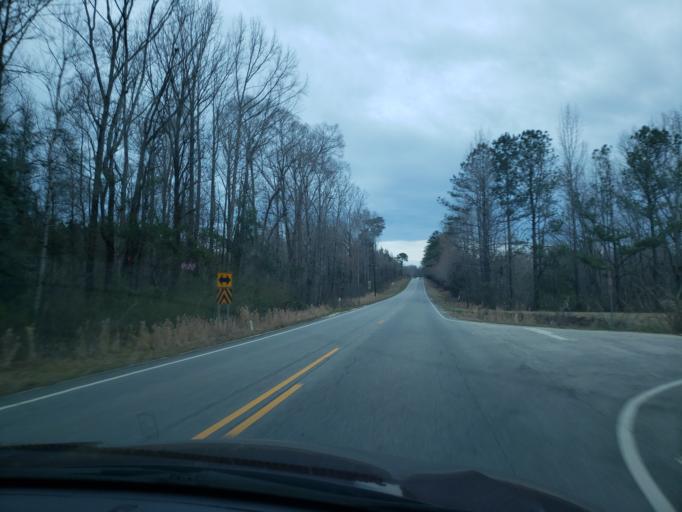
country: US
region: Alabama
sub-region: Chambers County
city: Lafayette
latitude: 32.9711
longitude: -85.4033
